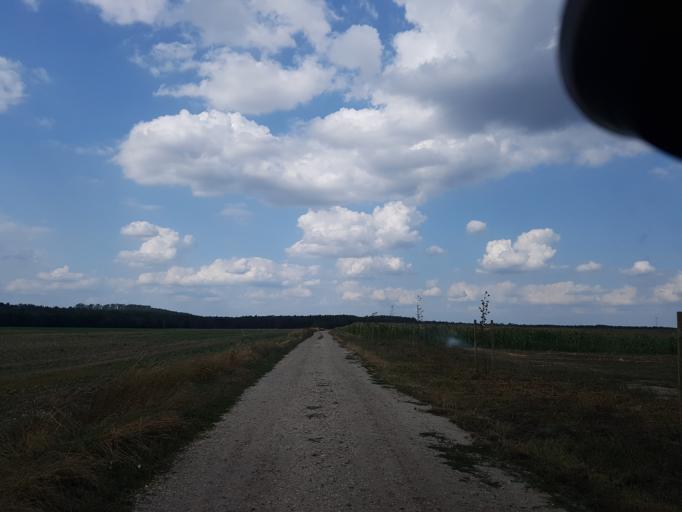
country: DE
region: Brandenburg
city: Calau
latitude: 51.7536
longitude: 13.9518
